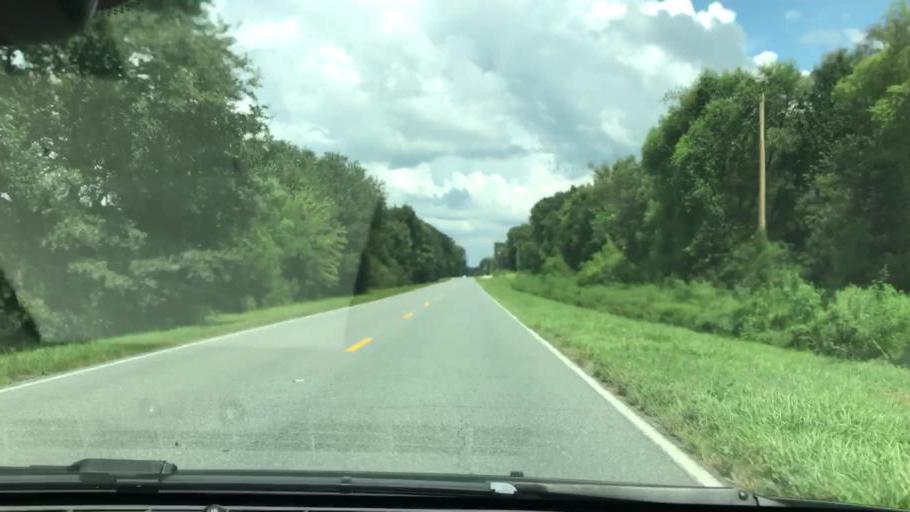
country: US
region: Florida
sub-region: Jackson County
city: Malone
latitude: 30.9005
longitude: -85.1345
